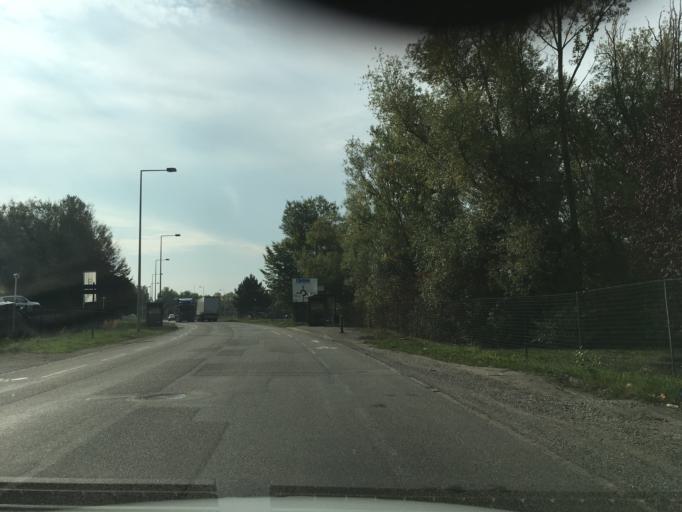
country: FR
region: Alsace
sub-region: Departement du Haut-Rhin
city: Houssen
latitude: 48.1046
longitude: 7.3787
